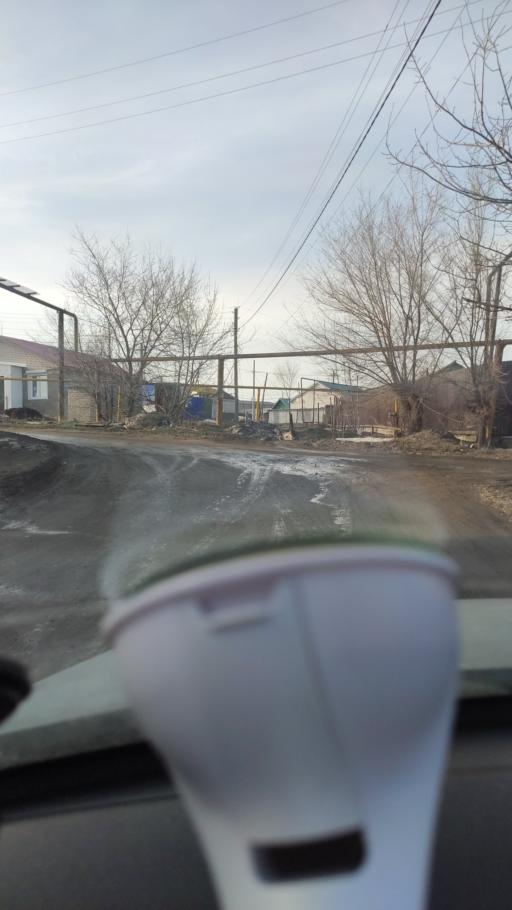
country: RU
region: Samara
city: Smyshlyayevka
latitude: 53.2439
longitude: 50.4874
